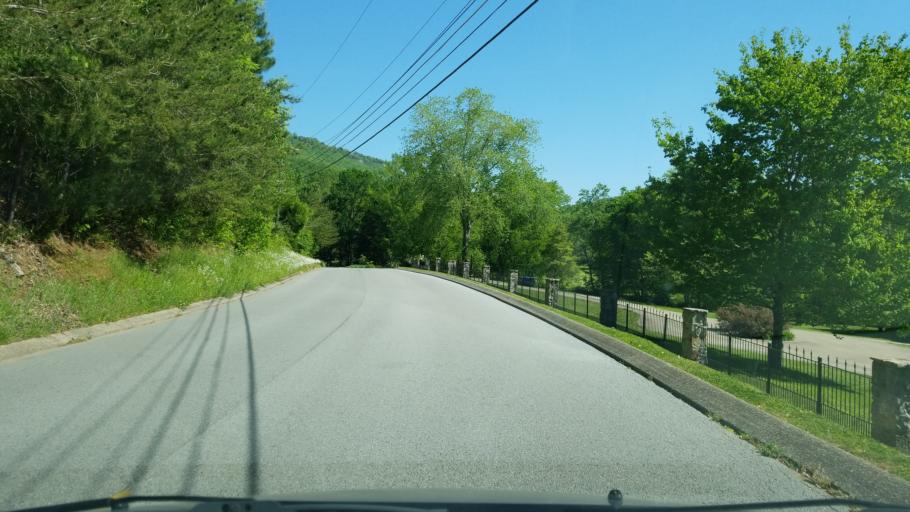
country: US
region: Tennessee
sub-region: Hamilton County
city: Walden
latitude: 35.1398
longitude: -85.3004
